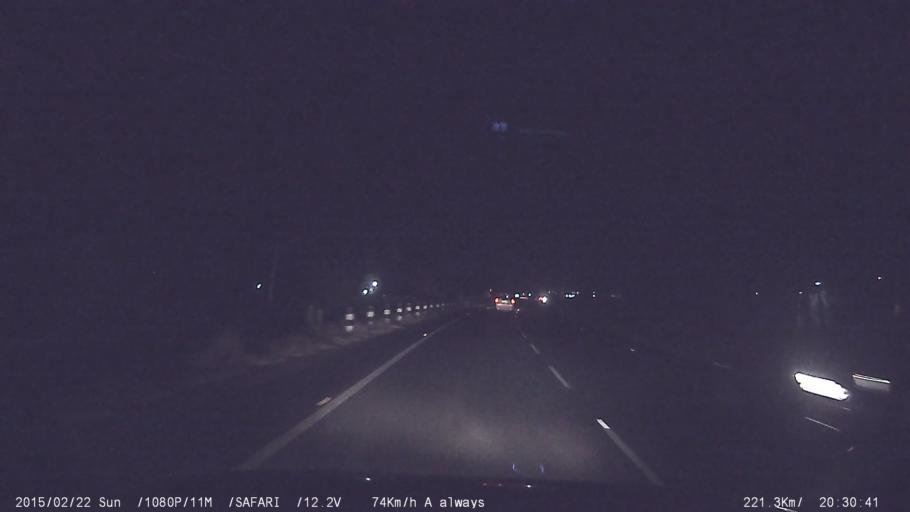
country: IN
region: Tamil Nadu
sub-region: Dindigul
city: Dindigul
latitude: 10.3403
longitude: 77.9414
